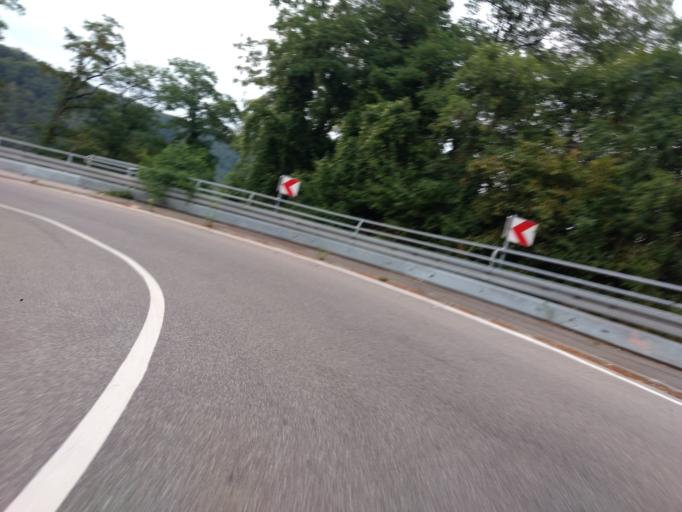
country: DE
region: Saarland
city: Wallerfangen
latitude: 49.3299
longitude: 6.6922
